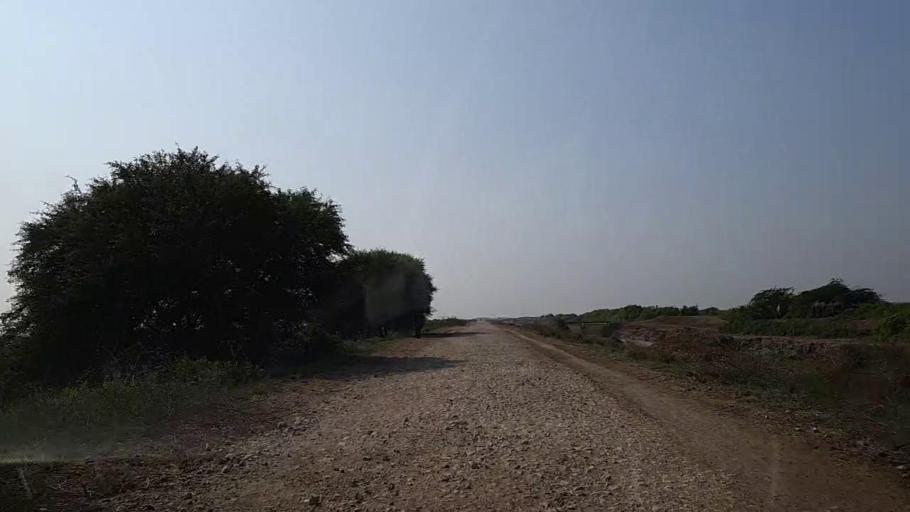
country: PK
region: Sindh
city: Mirpur Sakro
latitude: 24.6359
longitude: 67.7273
